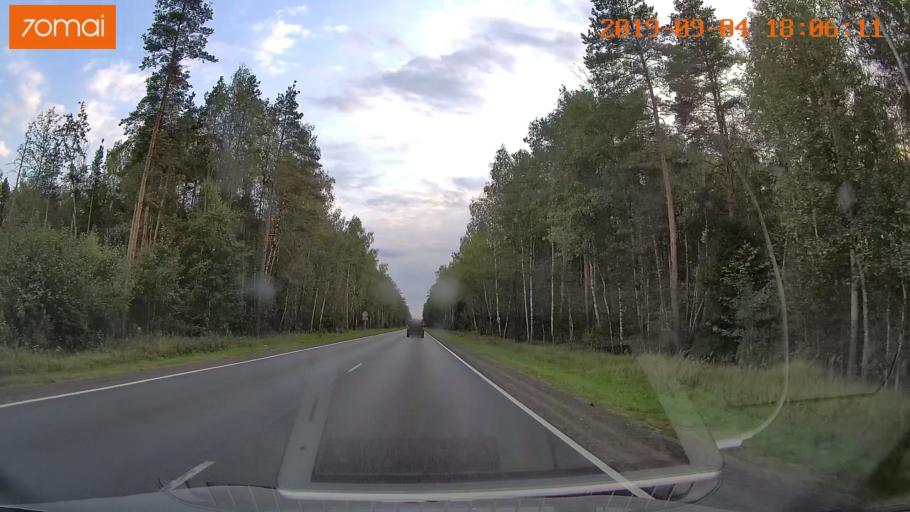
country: RU
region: Moskovskaya
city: Khorlovo
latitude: 55.4336
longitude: 38.8177
